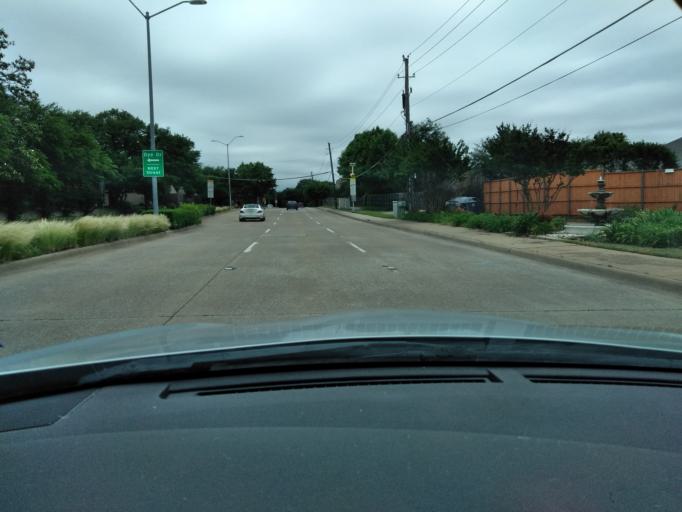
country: US
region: Texas
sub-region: Dallas County
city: Addison
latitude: 32.9833
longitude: -96.7859
